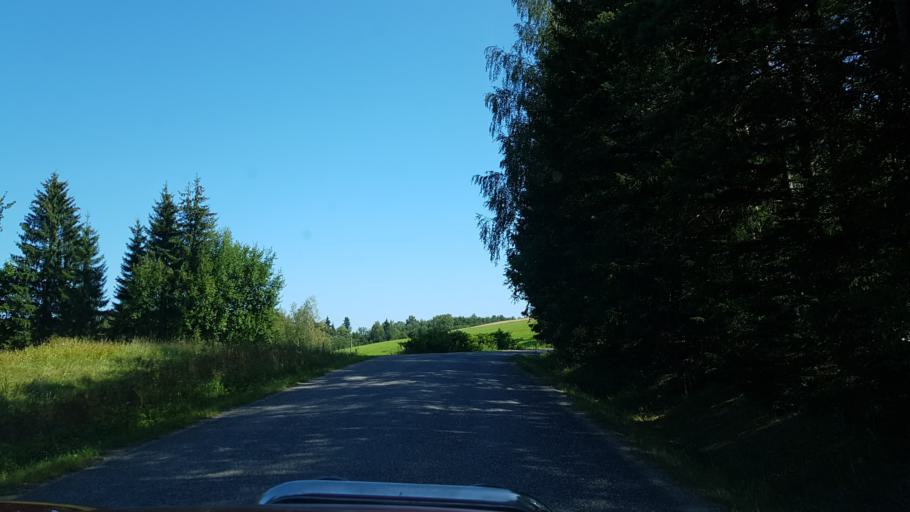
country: EE
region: Vorumaa
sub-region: Voru linn
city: Voru
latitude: 57.7202
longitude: 27.1009
